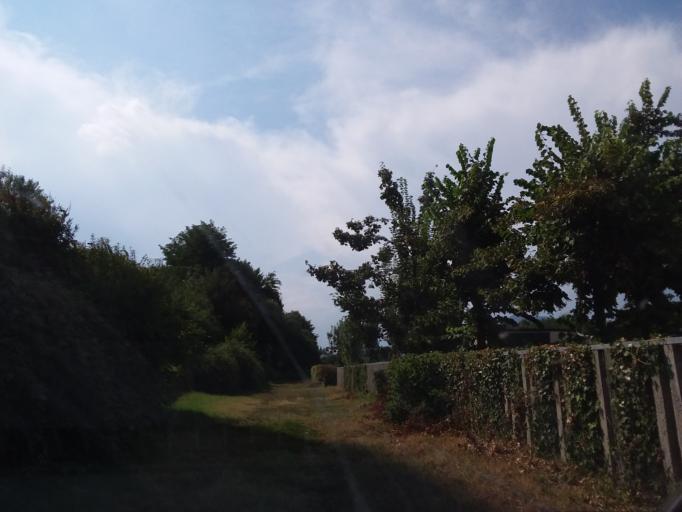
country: IT
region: Piedmont
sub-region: Provincia di Torino
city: Rivoli
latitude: 45.0741
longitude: 7.5353
